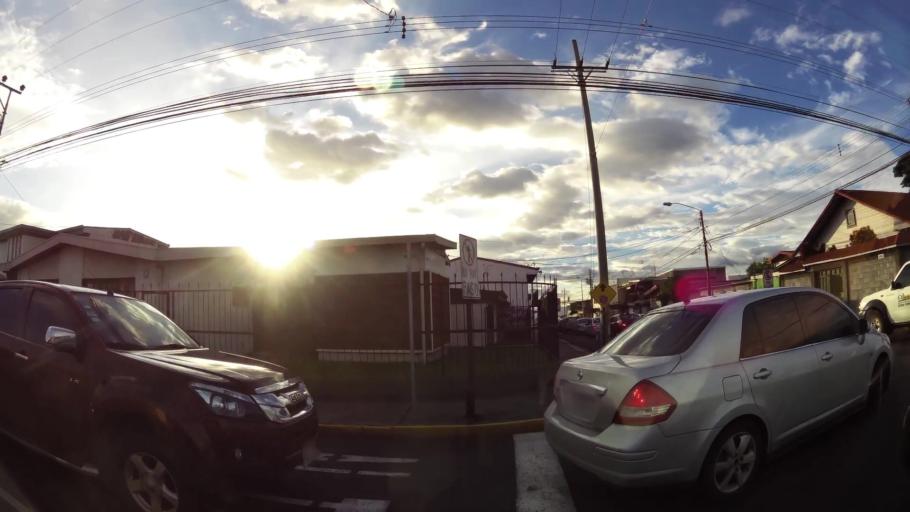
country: CR
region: Heredia
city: Heredia
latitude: 10.0008
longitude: -84.1209
